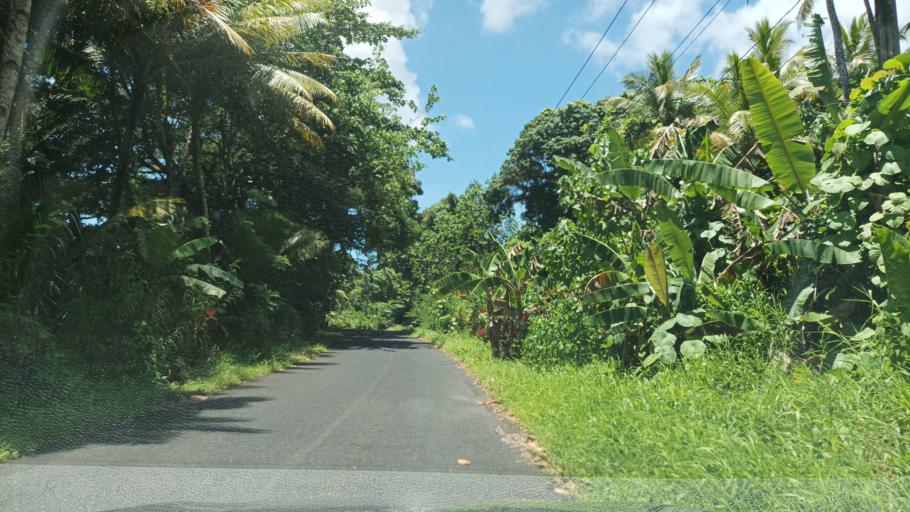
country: FM
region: Pohnpei
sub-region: Madolenihm Municipality
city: Madolenihm Municipality Government
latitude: 6.8525
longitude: 158.2972
